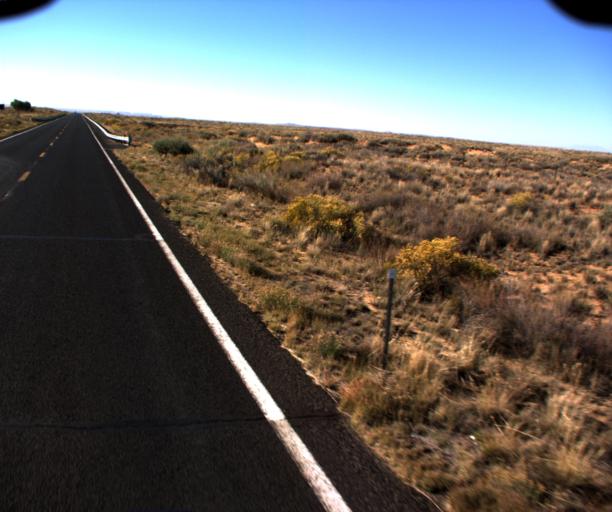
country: US
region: Arizona
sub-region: Navajo County
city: First Mesa
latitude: 35.7758
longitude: -110.5039
